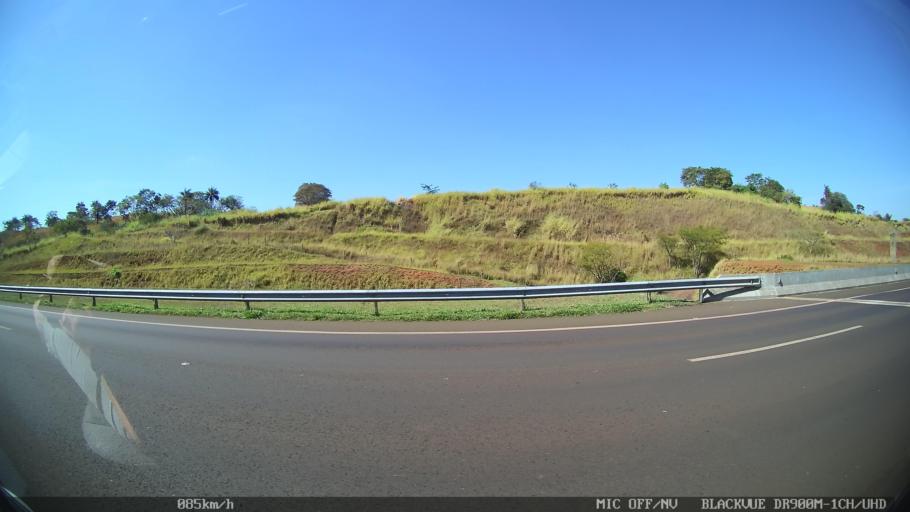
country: BR
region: Sao Paulo
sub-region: Franca
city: Franca
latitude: -20.6095
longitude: -47.4542
